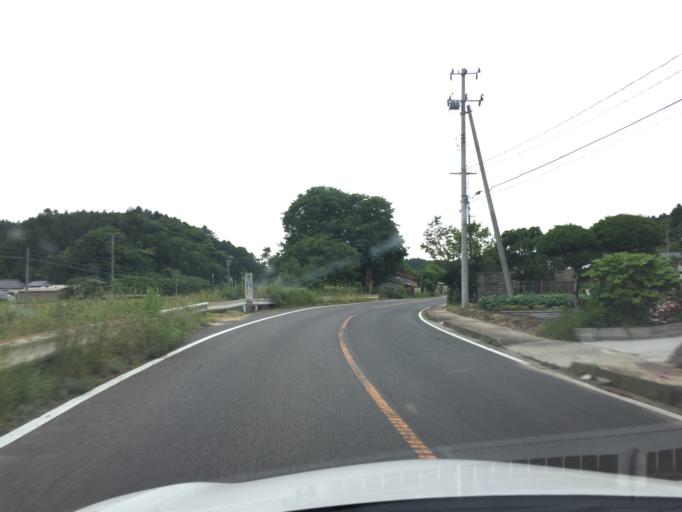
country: JP
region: Fukushima
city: Funehikimachi-funehiki
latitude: 37.3081
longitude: 140.6566
